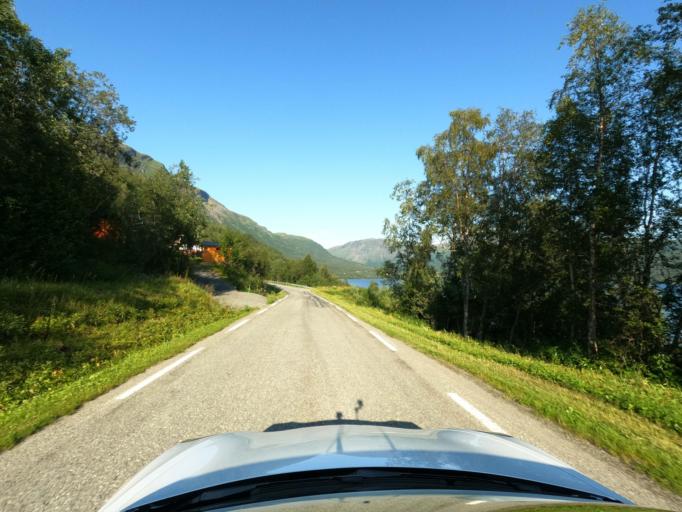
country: NO
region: Troms
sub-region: Gratangen
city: Gratangen
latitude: 68.5588
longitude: 17.6579
